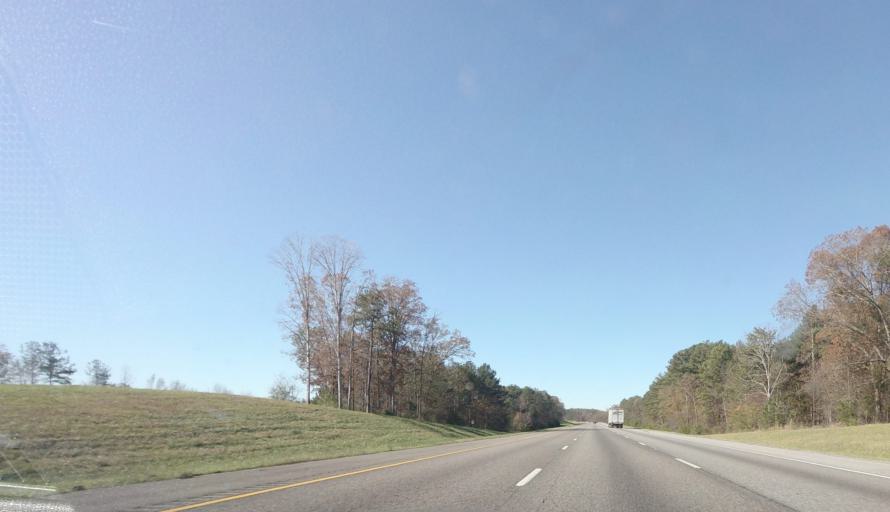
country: US
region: Alabama
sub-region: Calhoun County
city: Bynum
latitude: 33.5814
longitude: -85.9558
